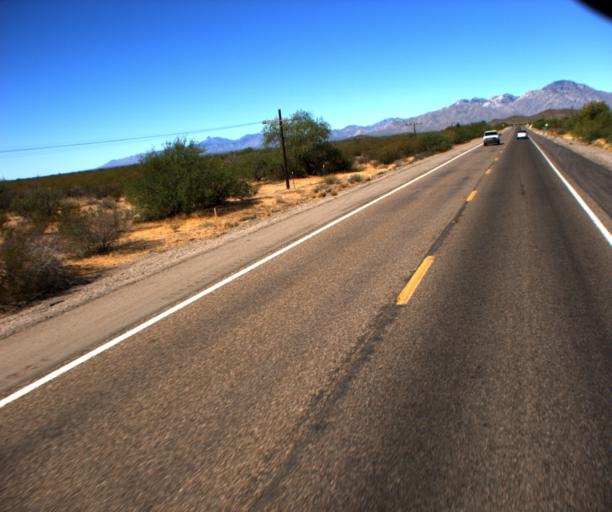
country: US
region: Arizona
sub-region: Pima County
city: Three Points
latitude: 32.0697
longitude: -111.3592
